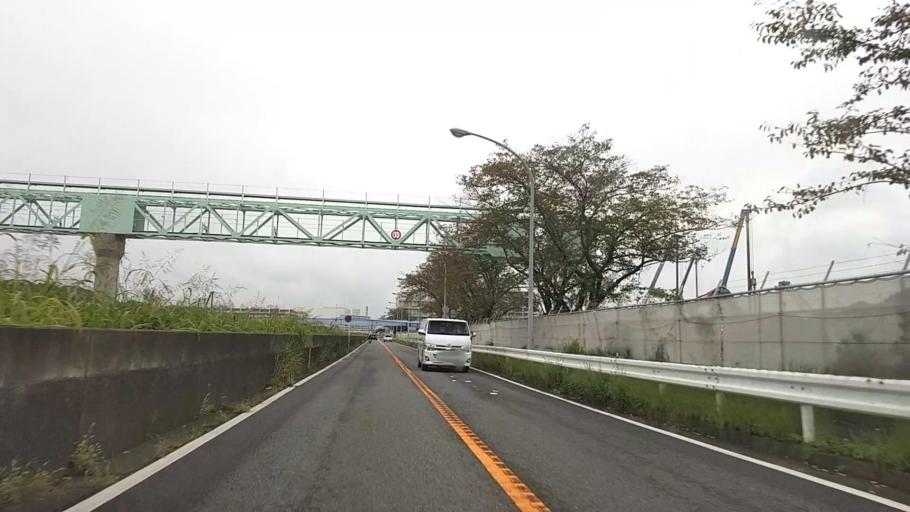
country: JP
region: Kanagawa
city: Fujisawa
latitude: 35.3907
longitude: 139.5331
